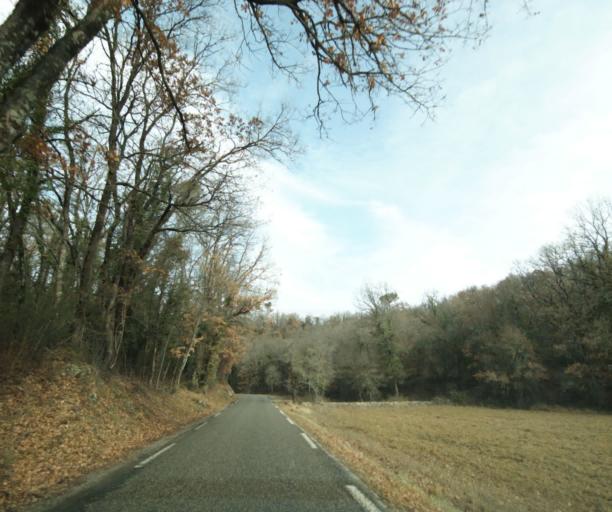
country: FR
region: Provence-Alpes-Cote d'Azur
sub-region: Departement du Var
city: Rougiers
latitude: 43.4163
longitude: 5.8700
